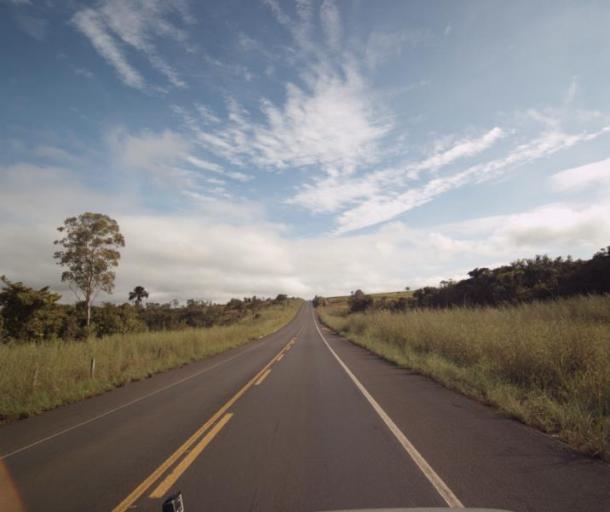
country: BR
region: Goias
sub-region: Padre Bernardo
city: Padre Bernardo
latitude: -15.4358
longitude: -48.6199
